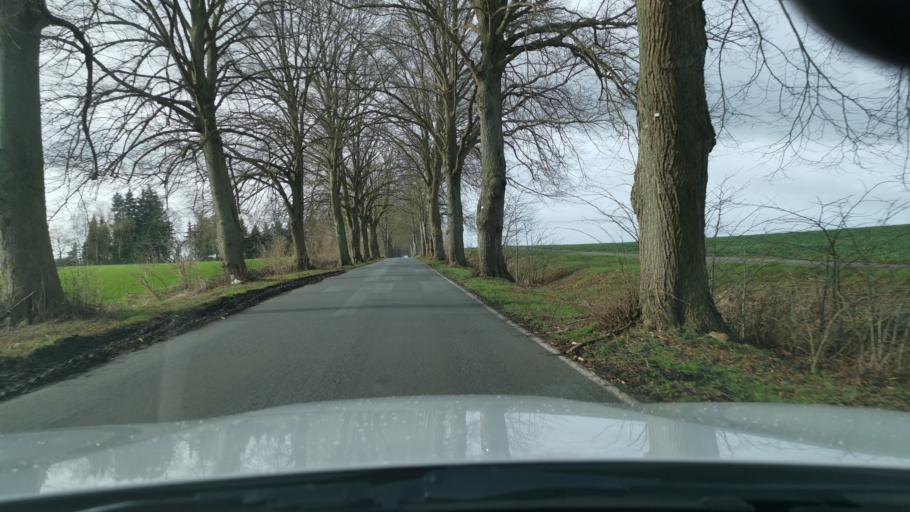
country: DE
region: Mecklenburg-Vorpommern
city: Wardow
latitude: 53.9990
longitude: 12.3825
